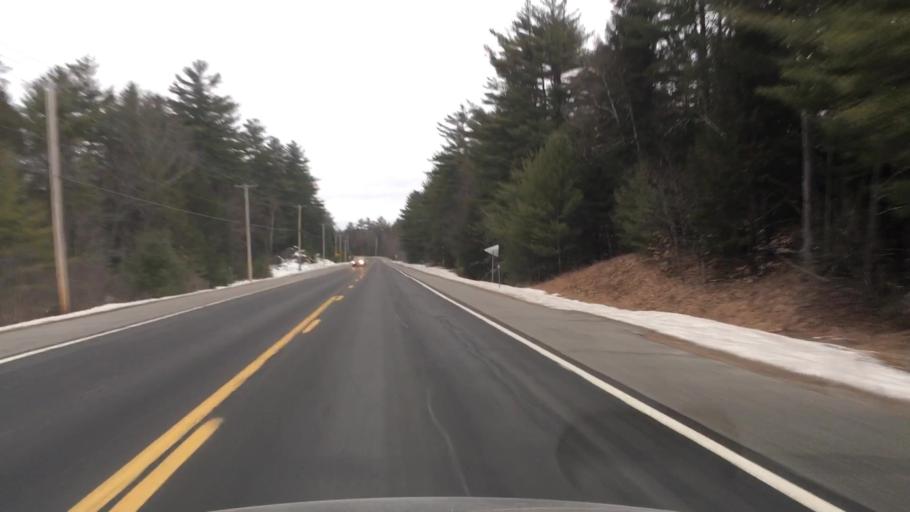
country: US
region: New Hampshire
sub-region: Merrimack County
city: Henniker
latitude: 43.2135
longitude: -71.8682
